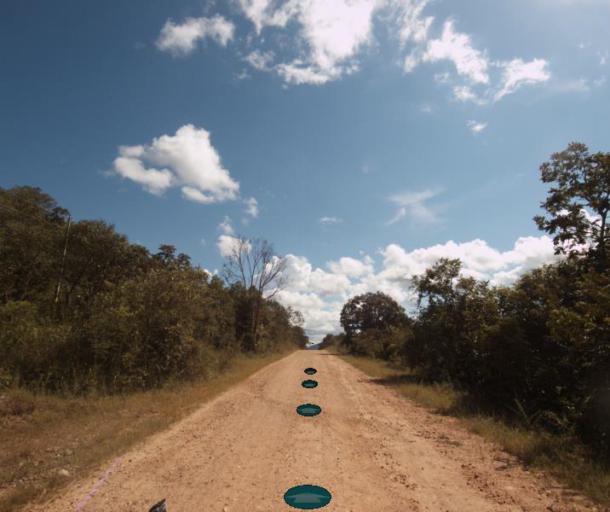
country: BR
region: Goias
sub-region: Pirenopolis
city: Pirenopolis
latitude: -15.7860
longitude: -49.0609
